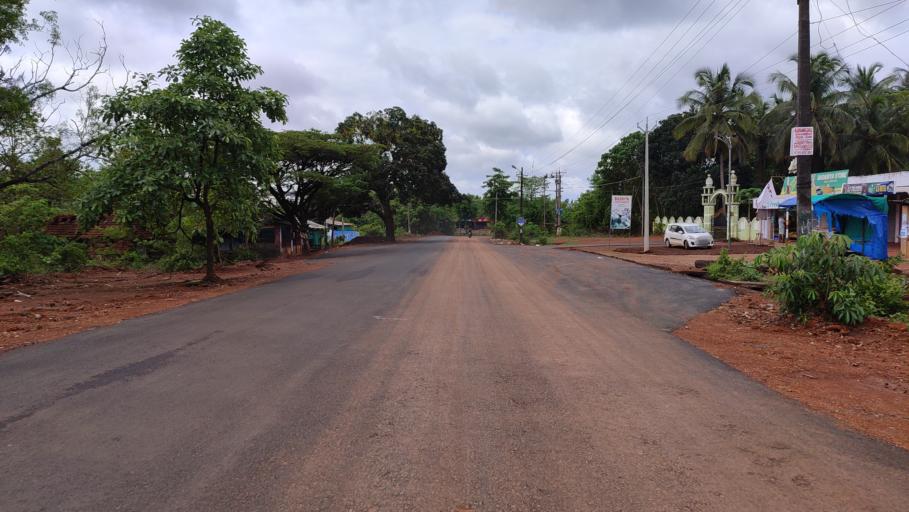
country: IN
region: Kerala
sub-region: Kasaragod District
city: Kasaragod
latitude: 12.5342
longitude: 75.0719
